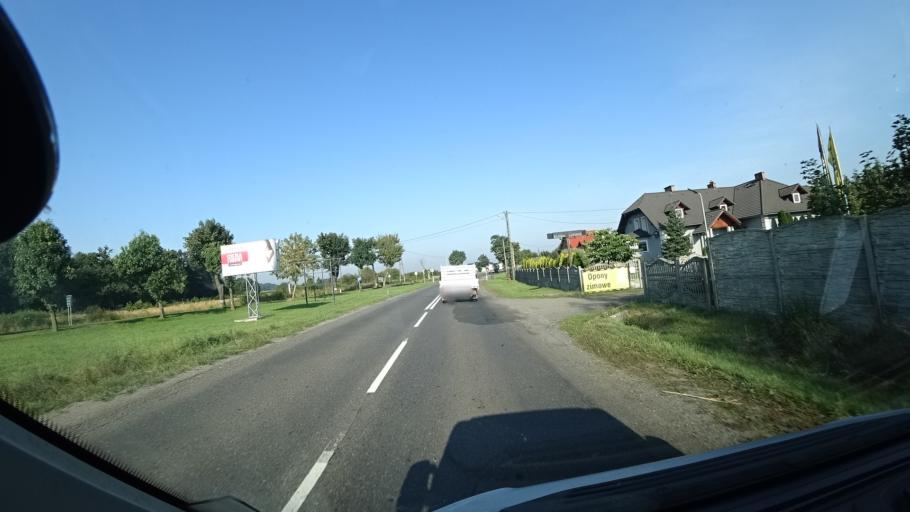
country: PL
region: Opole Voivodeship
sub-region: Powiat kedzierzynsko-kozielski
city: Kedzierzyn-Kozle
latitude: 50.3266
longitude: 18.2033
